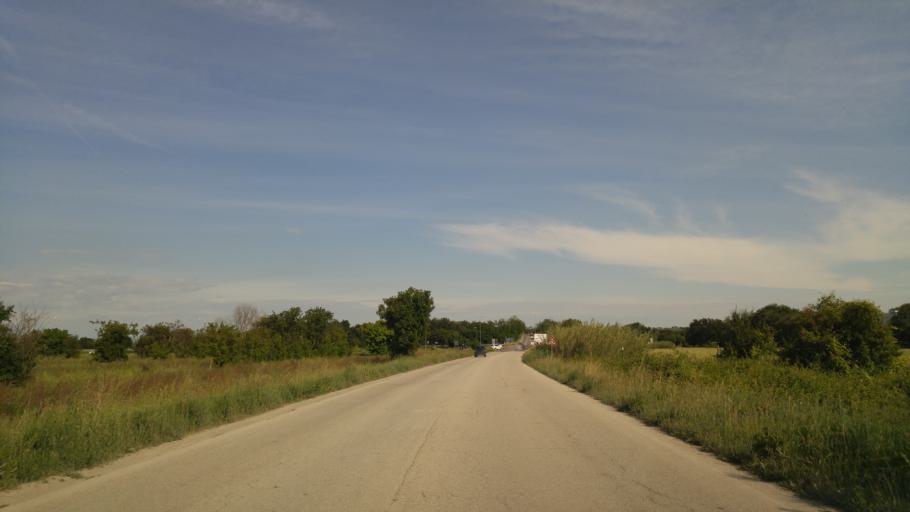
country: IT
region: The Marches
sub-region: Provincia di Pesaro e Urbino
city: Bellocchi
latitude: 43.8081
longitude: 13.0119
